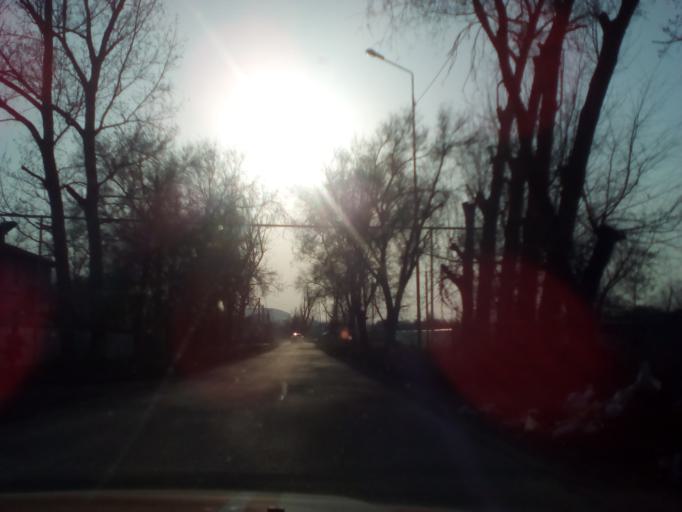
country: KZ
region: Almaty Oblysy
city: Burunday
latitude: 43.1595
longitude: 76.4465
